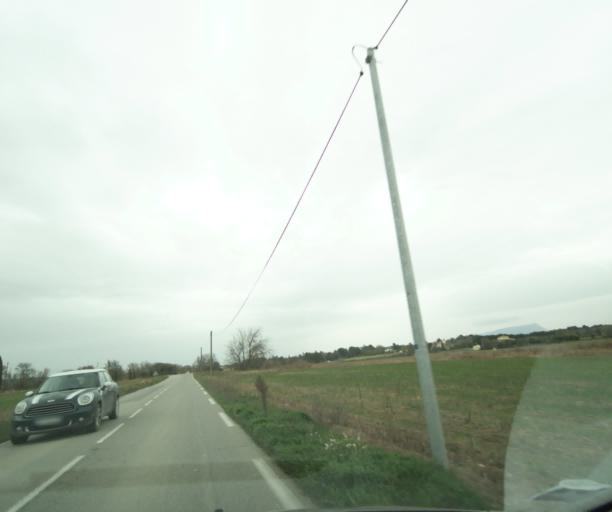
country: FR
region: Provence-Alpes-Cote d'Azur
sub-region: Departement des Bouches-du-Rhone
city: Eguilles
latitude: 43.5760
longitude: 5.4044
